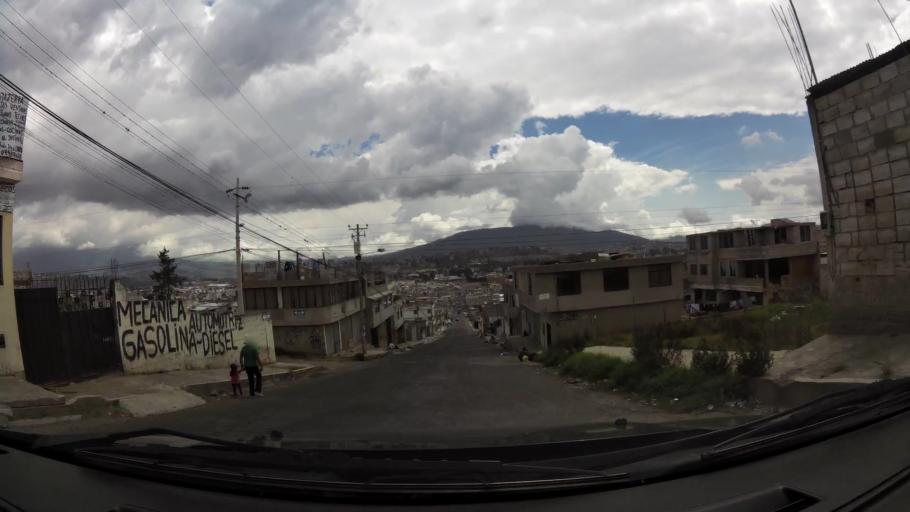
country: EC
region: Pichincha
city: Quito
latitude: -0.0816
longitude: -78.4099
